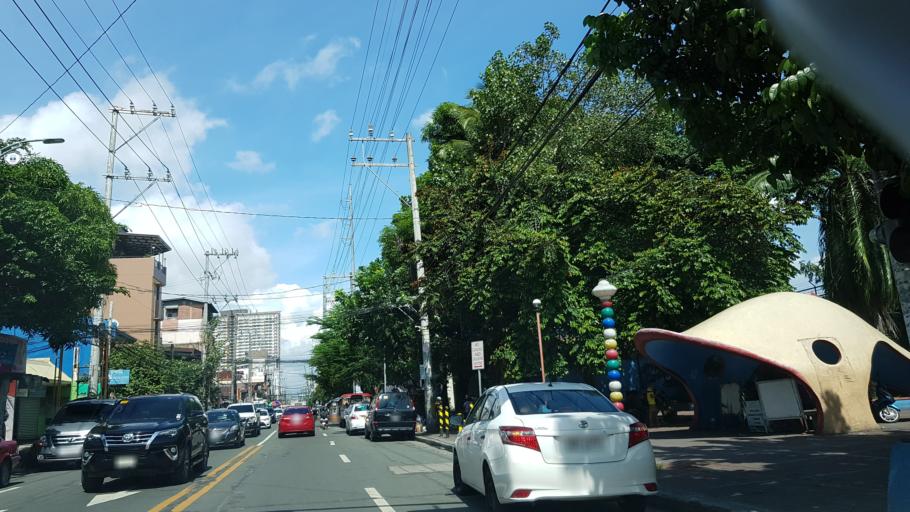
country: PH
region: Metro Manila
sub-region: City of Manila
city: Quiapo
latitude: 14.5791
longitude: 121.0032
